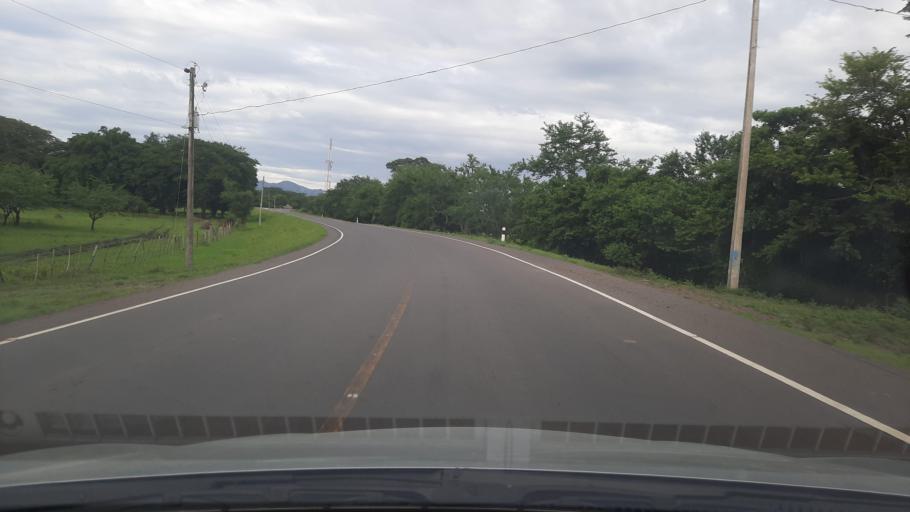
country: NI
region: Leon
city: Telica
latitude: 12.6506
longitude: -86.7454
